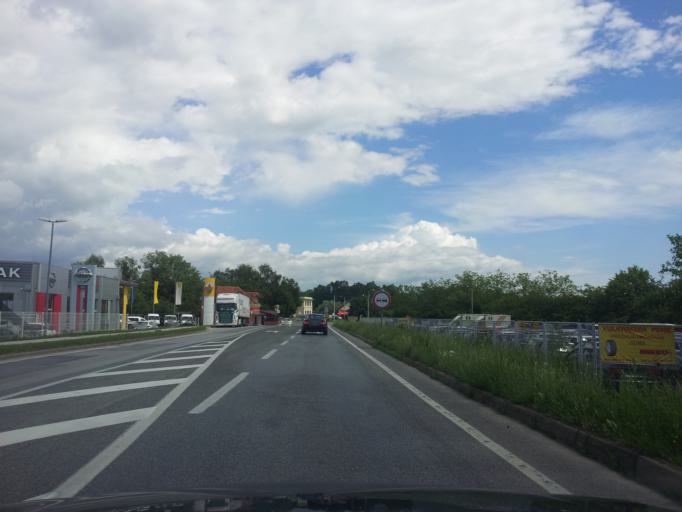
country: HR
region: Karlovacka
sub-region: Grad Karlovac
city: Karlovac
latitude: 45.5173
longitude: 15.5444
